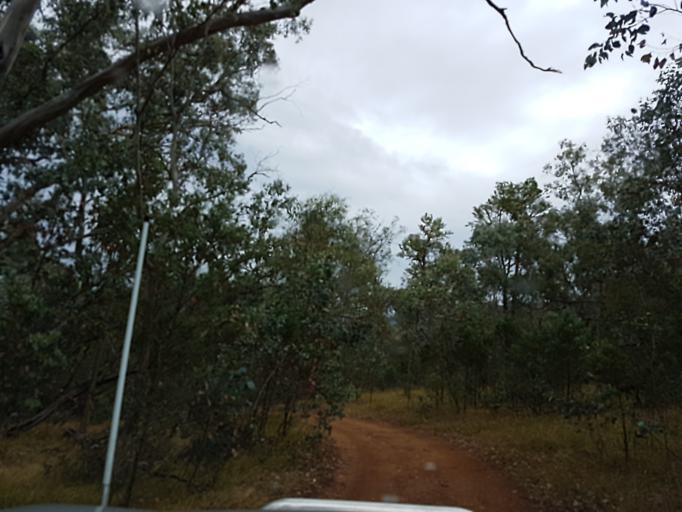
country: AU
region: New South Wales
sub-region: Snowy River
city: Jindabyne
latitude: -36.9423
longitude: 148.3951
